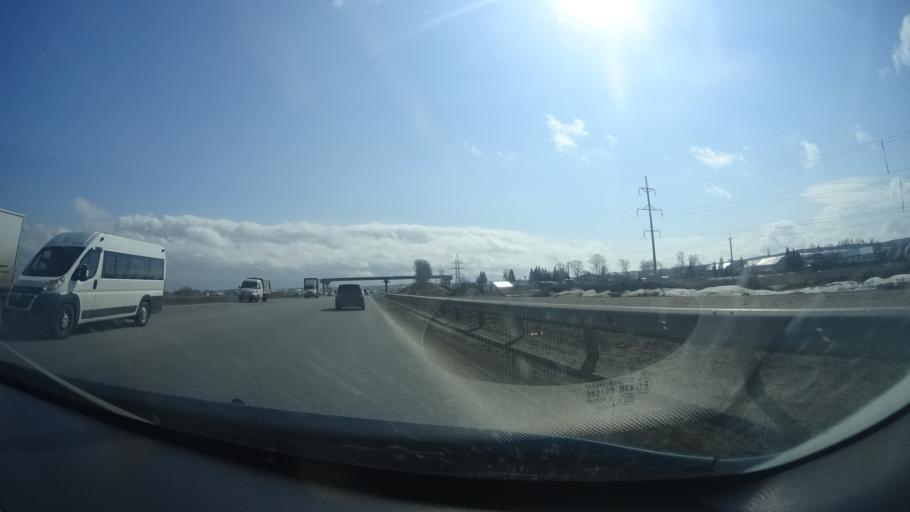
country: RU
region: Bashkortostan
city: Mikhaylovka
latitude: 54.8739
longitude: 55.7319
